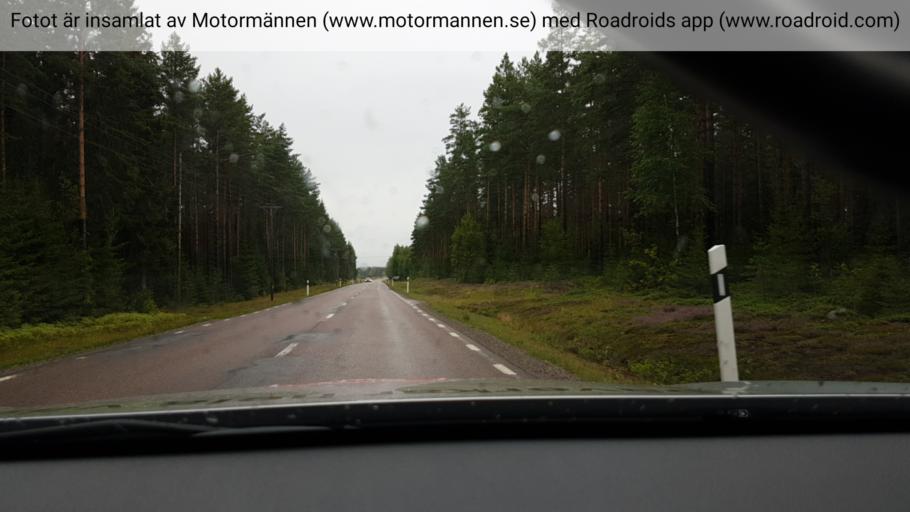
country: SE
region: Gaevleborg
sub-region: Gavle Kommun
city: Hedesunda
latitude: 60.4779
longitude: 16.9405
